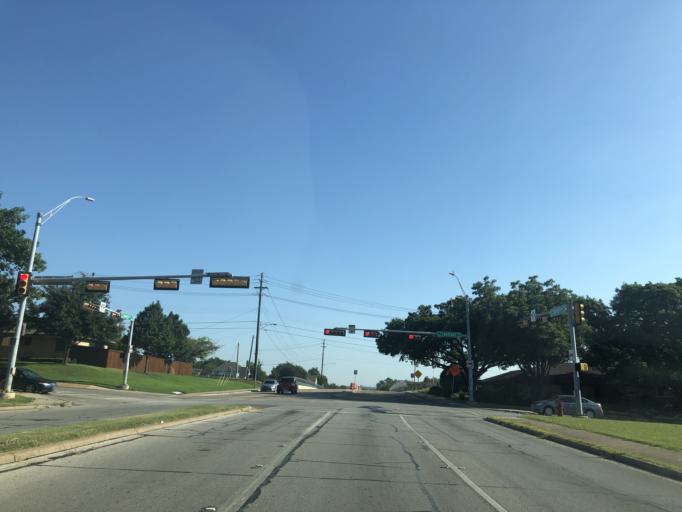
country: US
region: Texas
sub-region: Dallas County
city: Grand Prairie
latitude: 32.7580
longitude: -97.0198
